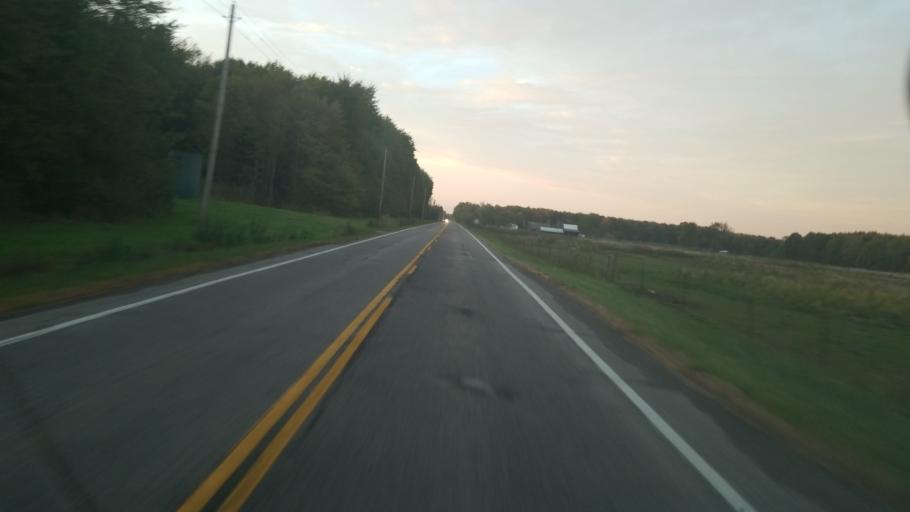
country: US
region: Ohio
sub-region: Ashtabula County
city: Andover
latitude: 41.6472
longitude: -80.6670
